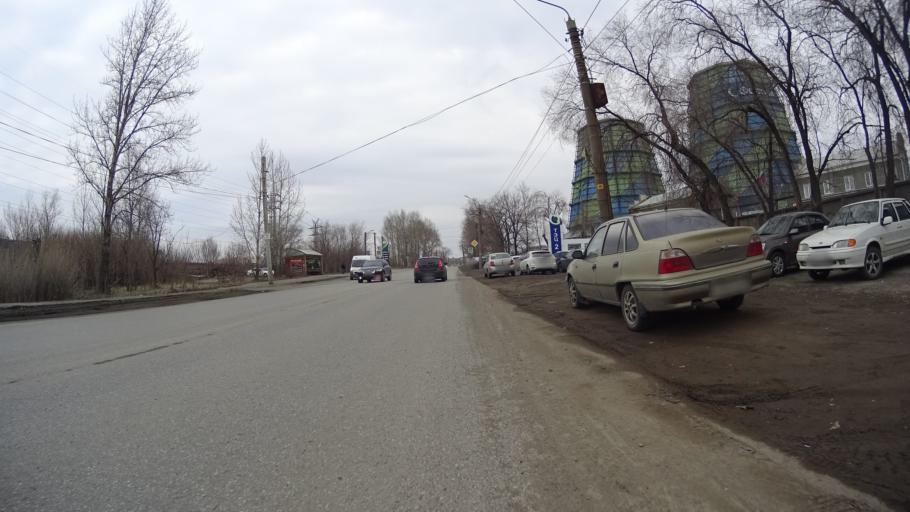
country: RU
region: Chelyabinsk
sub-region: Gorod Chelyabinsk
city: Chelyabinsk
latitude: 55.1563
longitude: 61.4982
